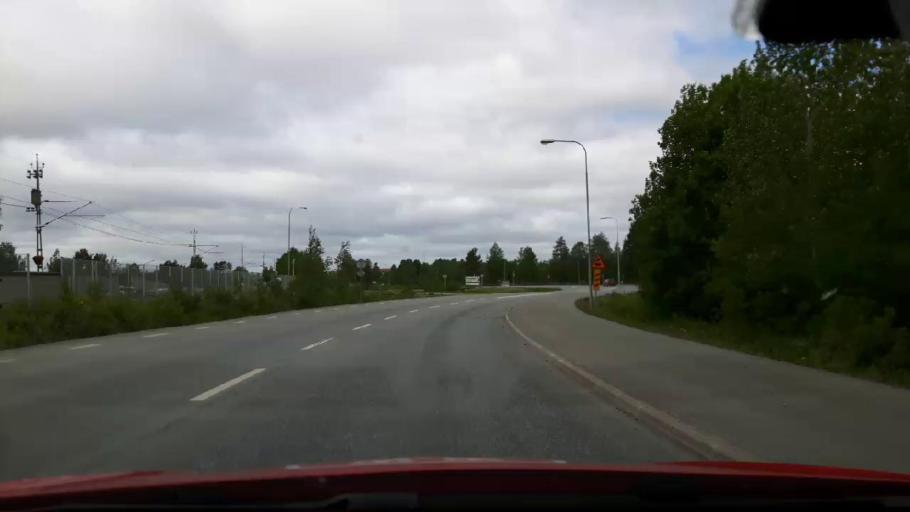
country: SE
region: Jaemtland
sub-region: Krokoms Kommun
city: Krokom
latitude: 63.3197
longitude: 14.4585
